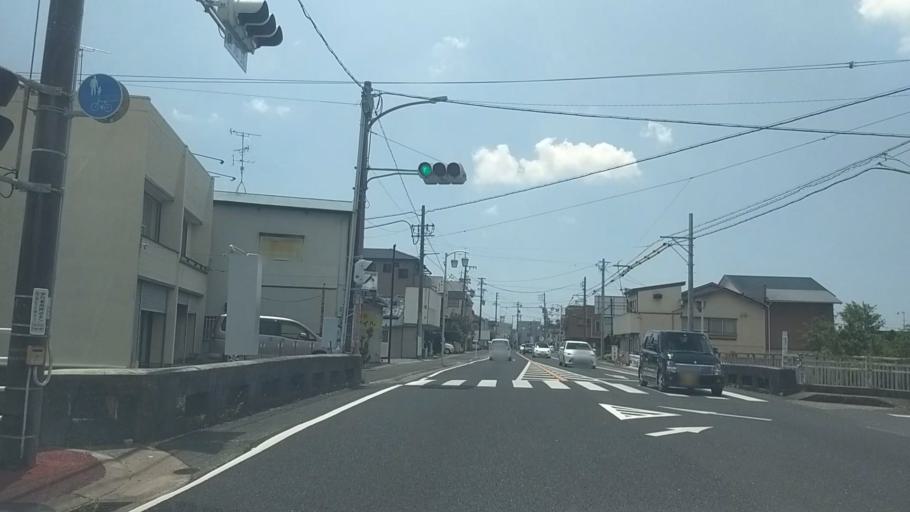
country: JP
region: Shizuoka
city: Hamamatsu
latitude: 34.7495
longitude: 137.7239
